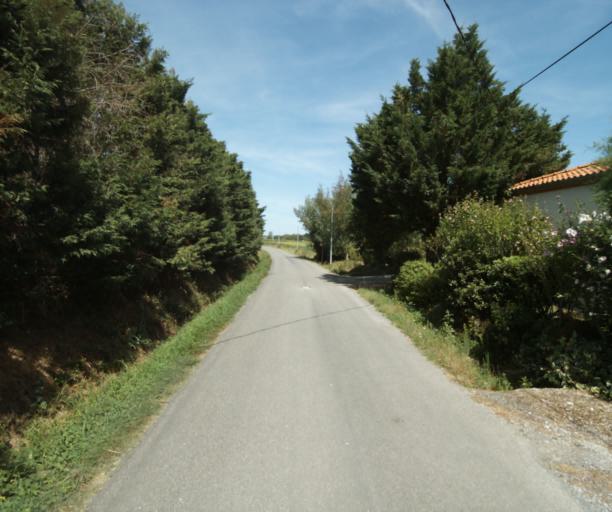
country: FR
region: Midi-Pyrenees
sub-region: Departement de la Haute-Garonne
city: Revel
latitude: 43.5004
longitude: 2.0247
